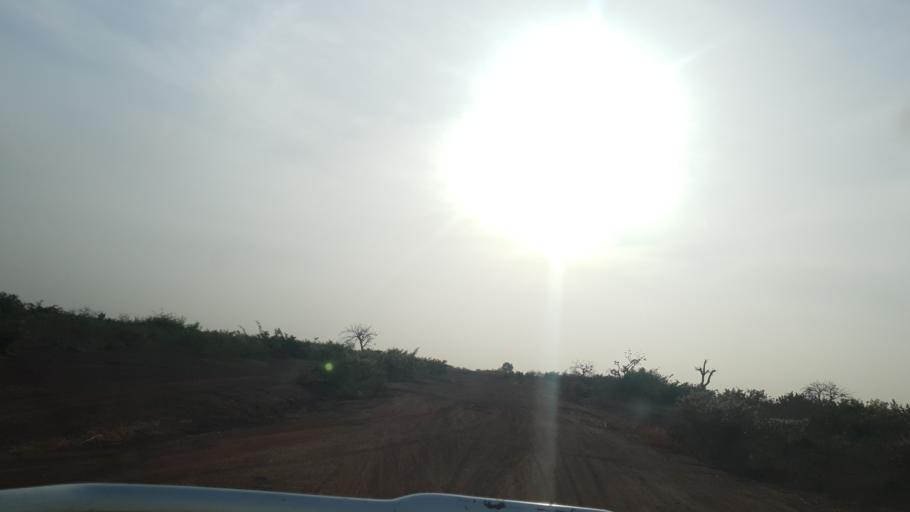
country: ML
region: Koulikoro
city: Dioila
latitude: 12.7676
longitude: -6.9220
